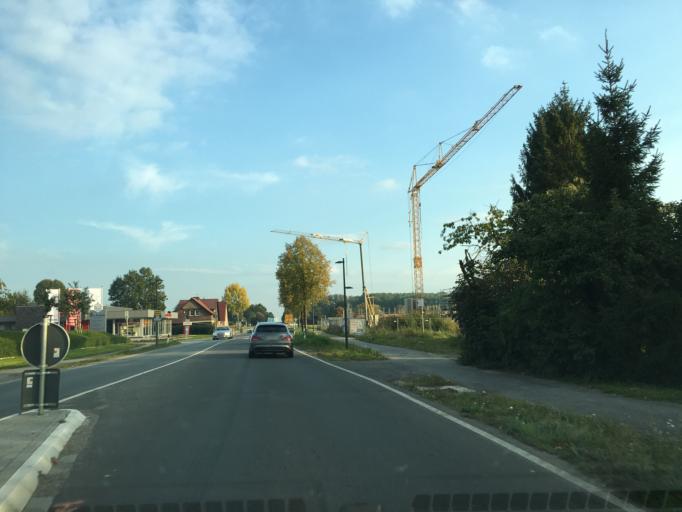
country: DE
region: North Rhine-Westphalia
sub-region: Regierungsbezirk Munster
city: Altenberge
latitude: 52.0395
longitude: 7.4721
